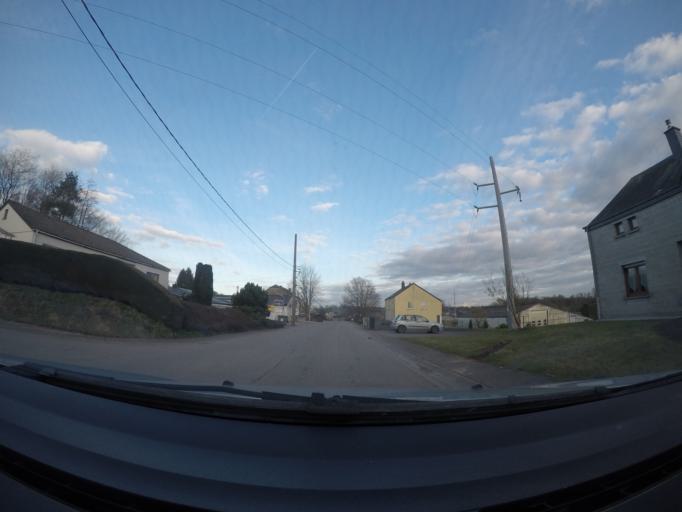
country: BE
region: Wallonia
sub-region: Province du Luxembourg
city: Tintigny
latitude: 49.6996
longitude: 5.5557
